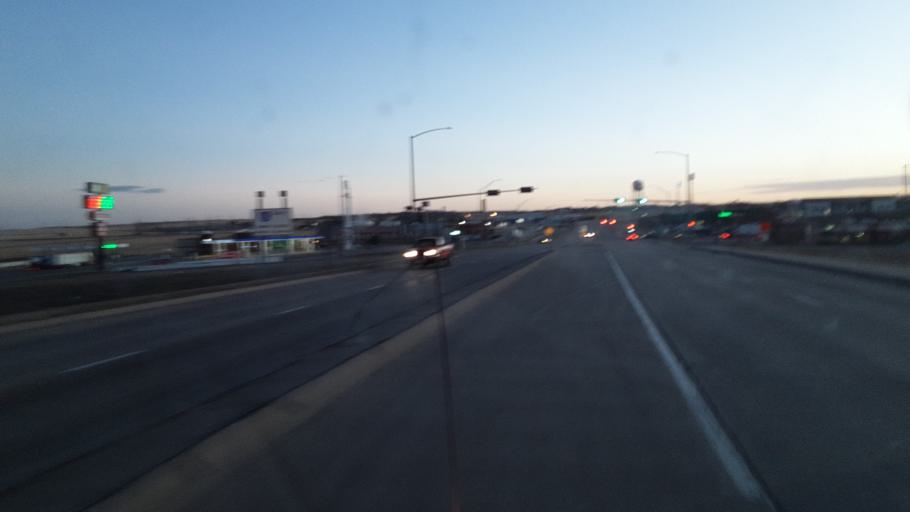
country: US
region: Nebraska
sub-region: Keith County
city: Ogallala
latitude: 41.1146
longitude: -101.7153
